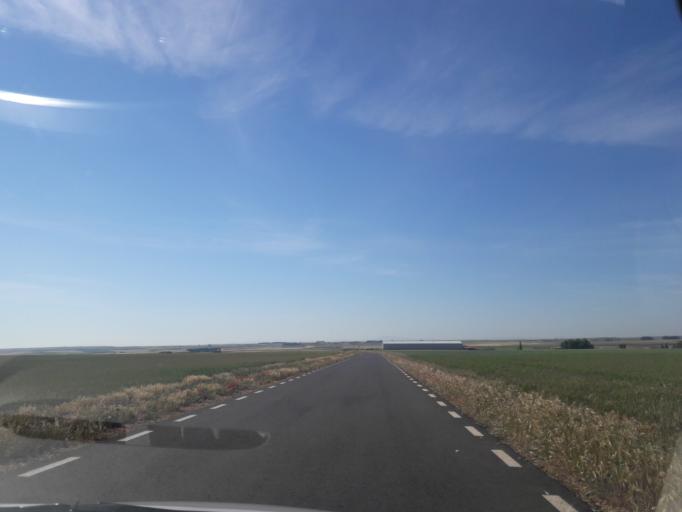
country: ES
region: Castille and Leon
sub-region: Provincia de Salamanca
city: Espino de la Orbada
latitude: 41.1152
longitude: -5.4247
